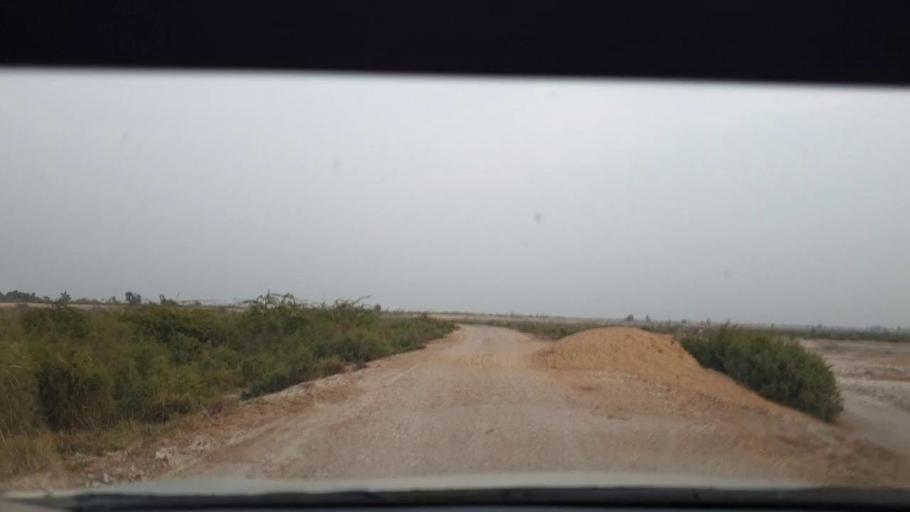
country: PK
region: Sindh
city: Berani
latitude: 25.8787
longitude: 68.7587
